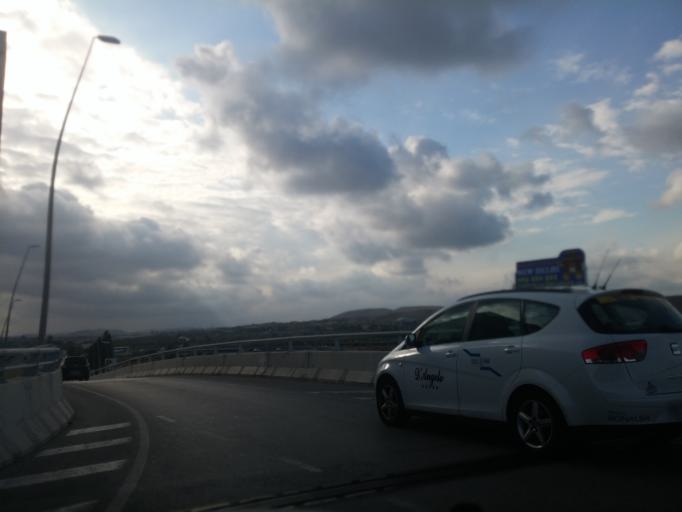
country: ES
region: Valencia
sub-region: Provincia de Alicante
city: Alicante
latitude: 38.2887
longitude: -0.5530
